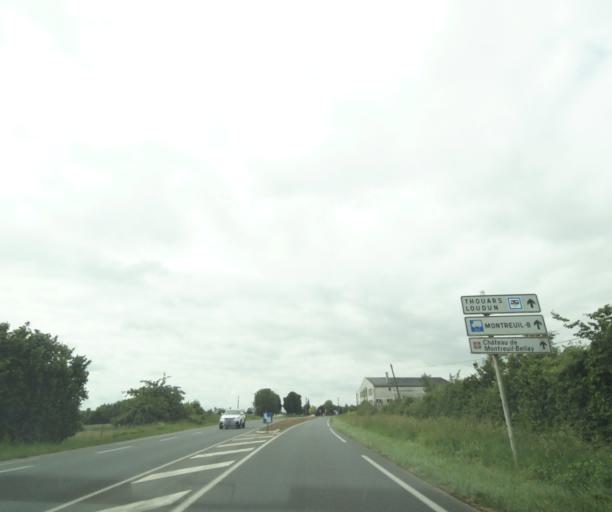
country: FR
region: Pays de la Loire
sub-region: Departement de Maine-et-Loire
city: Montreuil-Bellay
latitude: 47.1447
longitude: -0.1521
